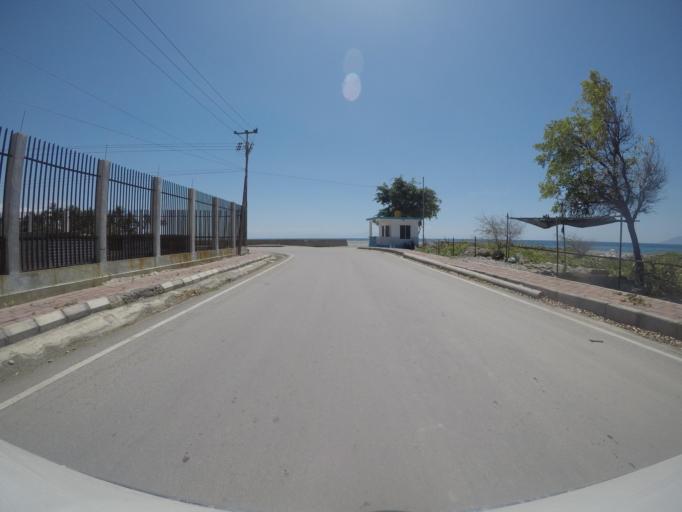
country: TL
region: Dili
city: Dili
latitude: -8.5385
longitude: 125.5355
